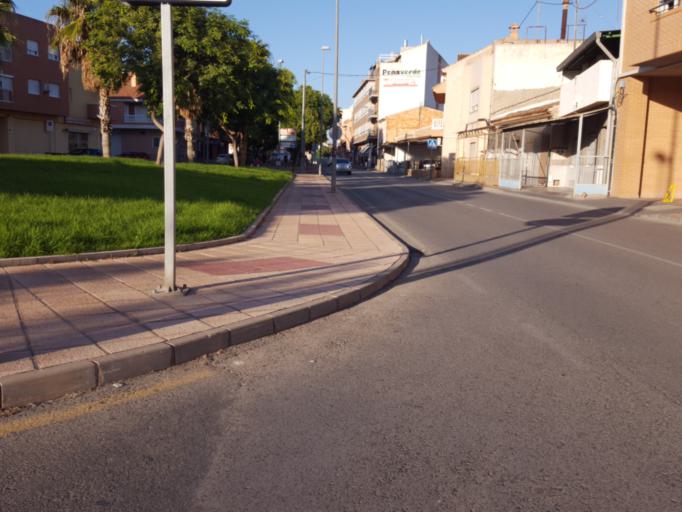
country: ES
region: Murcia
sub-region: Murcia
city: Murcia
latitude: 37.9964
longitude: -1.1754
